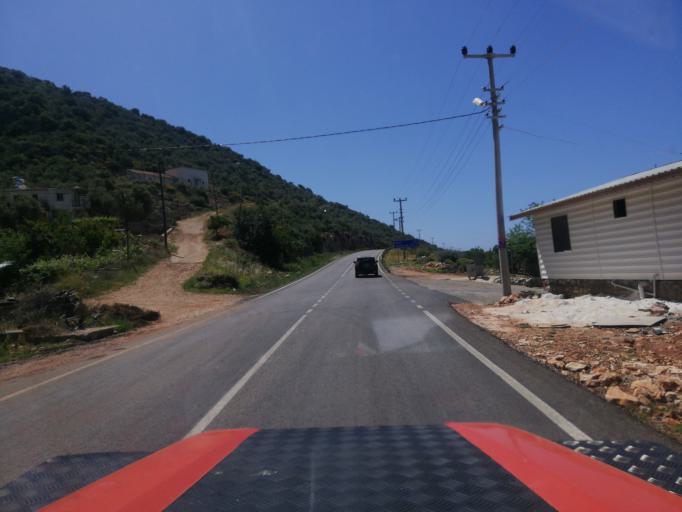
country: TR
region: Antalya
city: Kalkan
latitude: 36.2410
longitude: 29.4275
